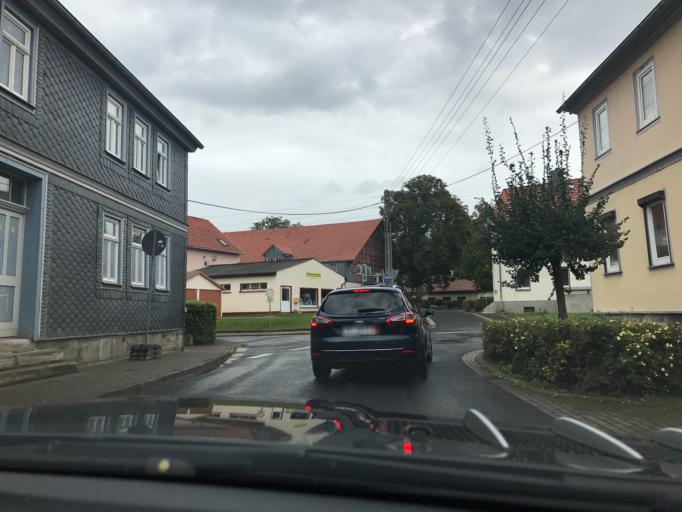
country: DE
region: Thuringia
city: Mulverstedt
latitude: 51.1190
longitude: 10.5043
